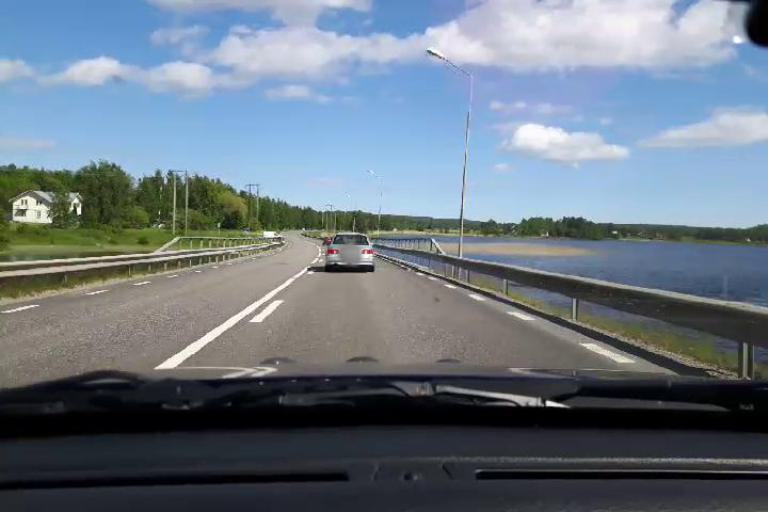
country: SE
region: Gaevleborg
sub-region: Hudiksvalls Kommun
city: Sorforsa
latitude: 61.7337
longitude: 16.9420
